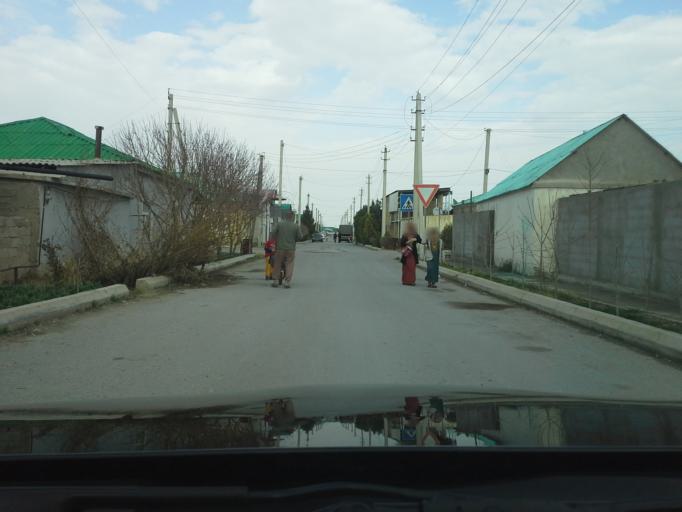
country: TM
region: Ahal
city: Abadan
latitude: 37.9897
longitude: 58.2816
